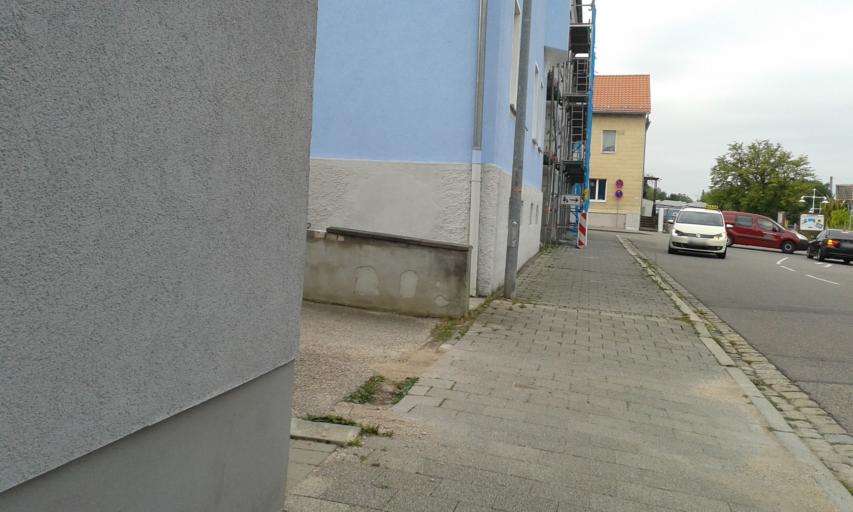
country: DE
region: Bavaria
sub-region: Regierungsbezirk Mittelfranken
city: Gunzenhausen
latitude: 49.1195
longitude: 10.7545
